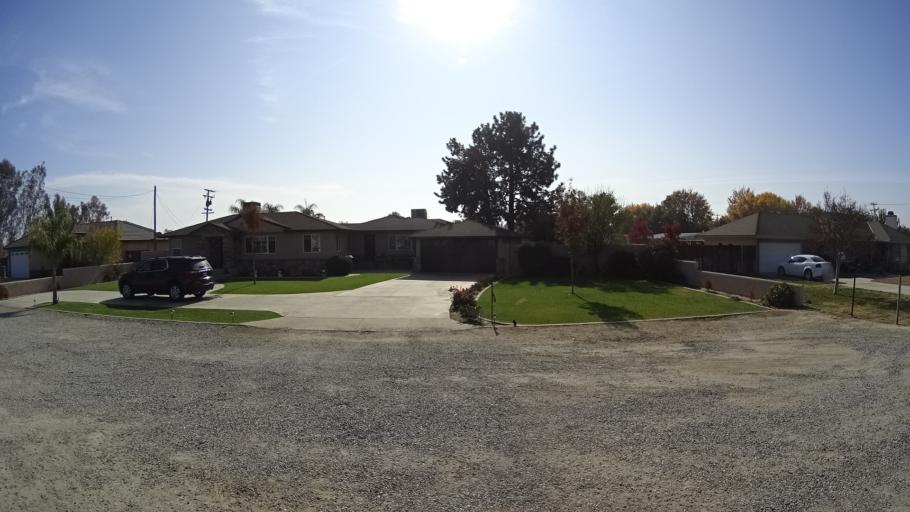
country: US
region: California
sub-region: Kern County
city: Rosedale
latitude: 35.3654
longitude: -119.1622
